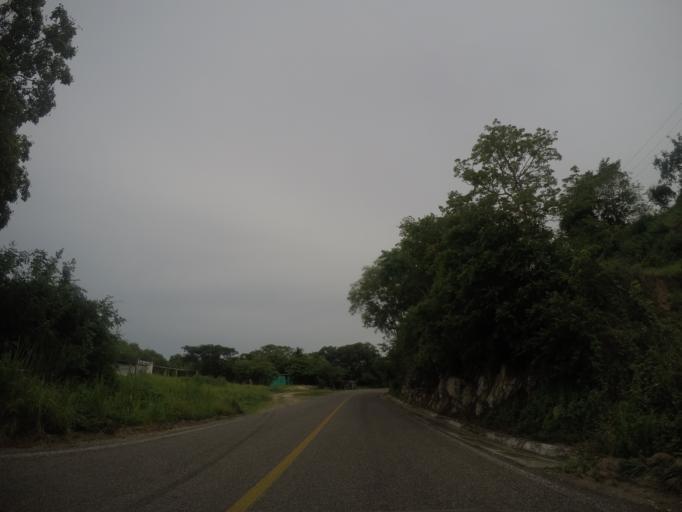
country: MX
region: Oaxaca
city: San Pedro Mixtepec
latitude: 15.9421
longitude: -97.1759
